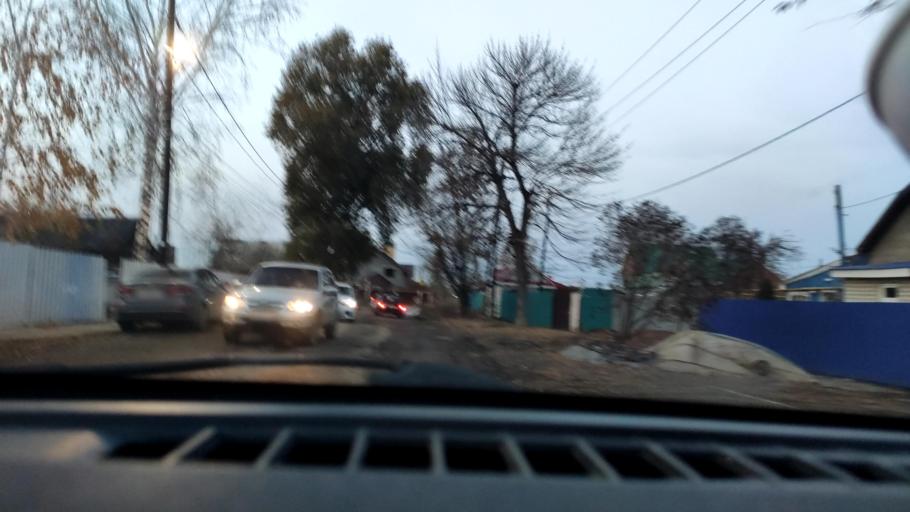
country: RU
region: Samara
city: Samara
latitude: 53.1343
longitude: 50.0949
